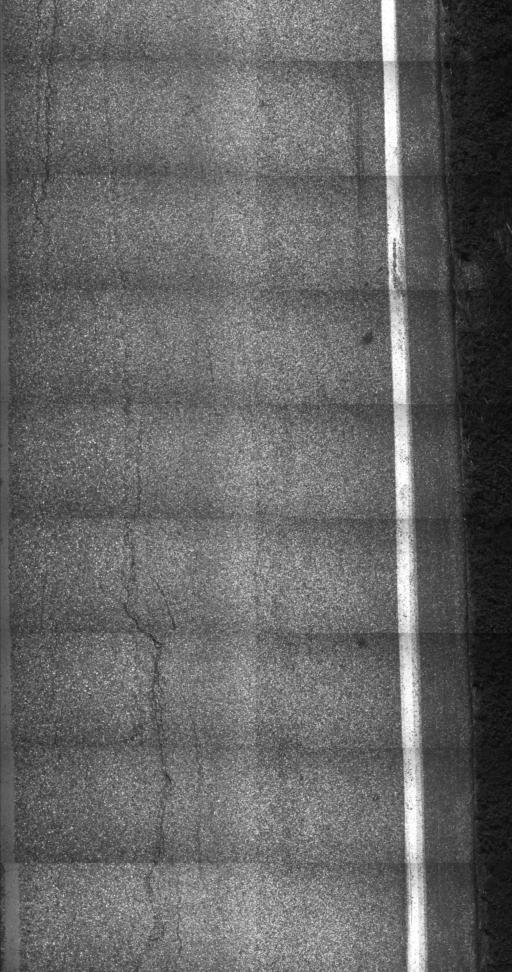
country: US
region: Vermont
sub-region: Bennington County
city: Manchester Center
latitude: 43.2603
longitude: -73.1037
